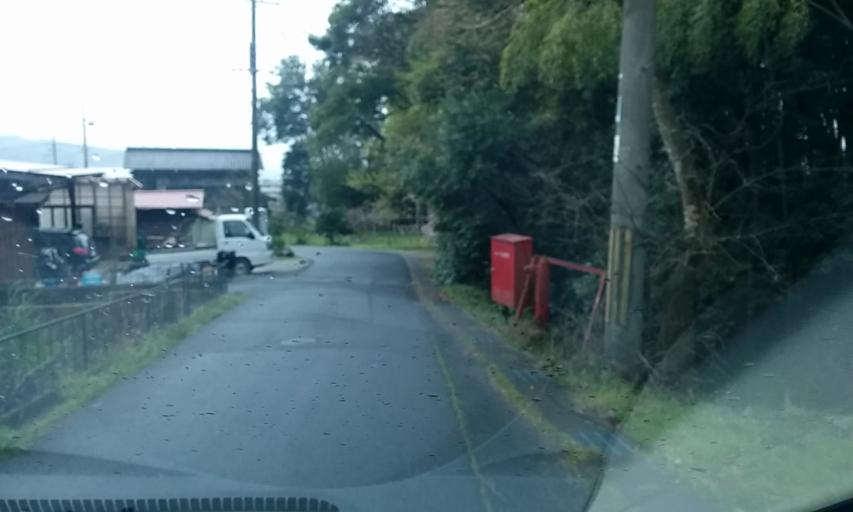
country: JP
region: Kyoto
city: Miyazu
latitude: 35.5847
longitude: 135.1984
